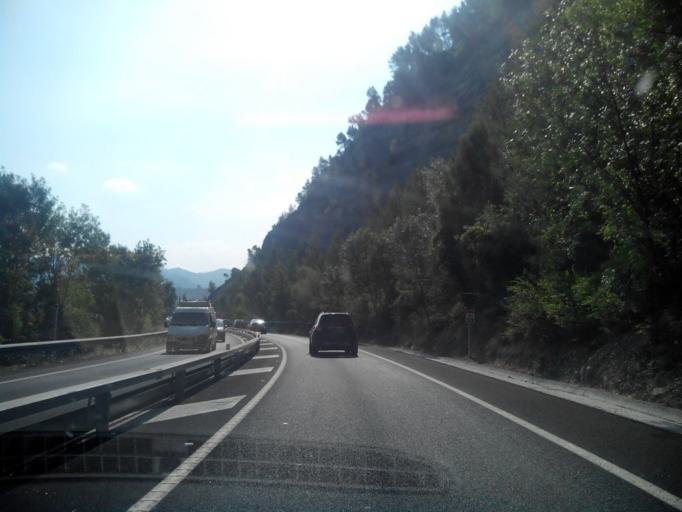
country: ES
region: Catalonia
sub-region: Provincia de Barcelona
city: Manresa
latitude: 41.6789
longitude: 1.8391
